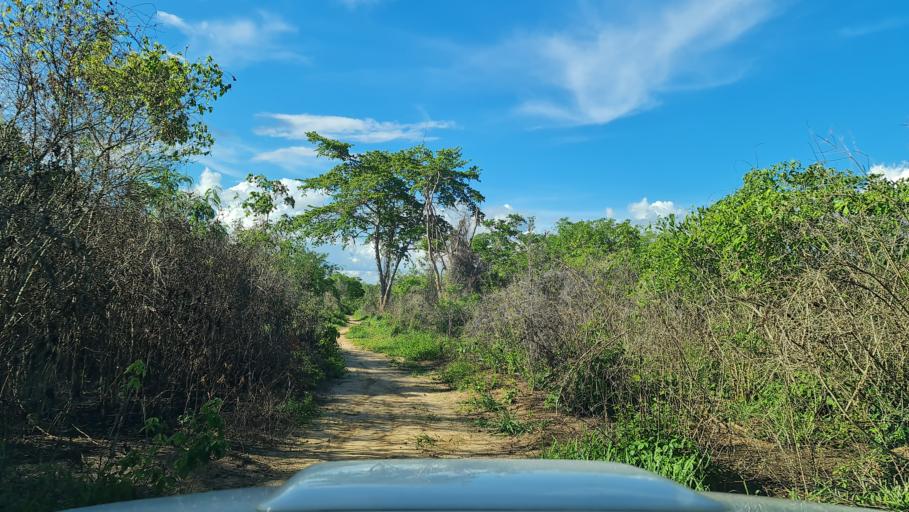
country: MZ
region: Nampula
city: Ilha de Mocambique
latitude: -15.2604
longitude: 40.1848
